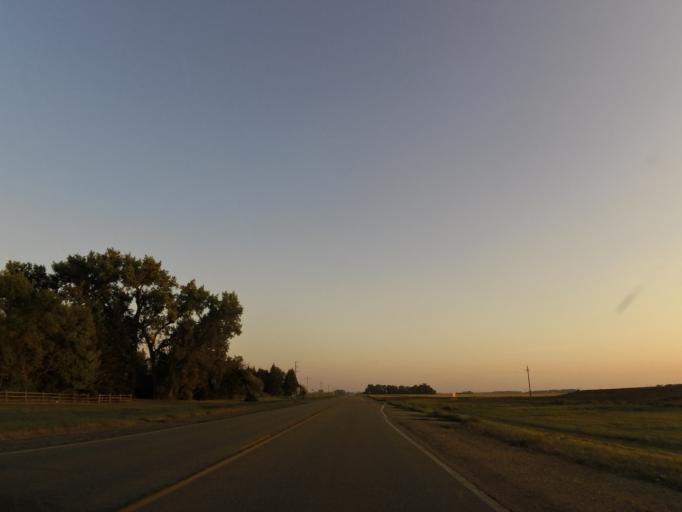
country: US
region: North Dakota
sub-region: Grand Forks County
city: Grand Forks
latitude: 47.8623
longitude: -97.0453
